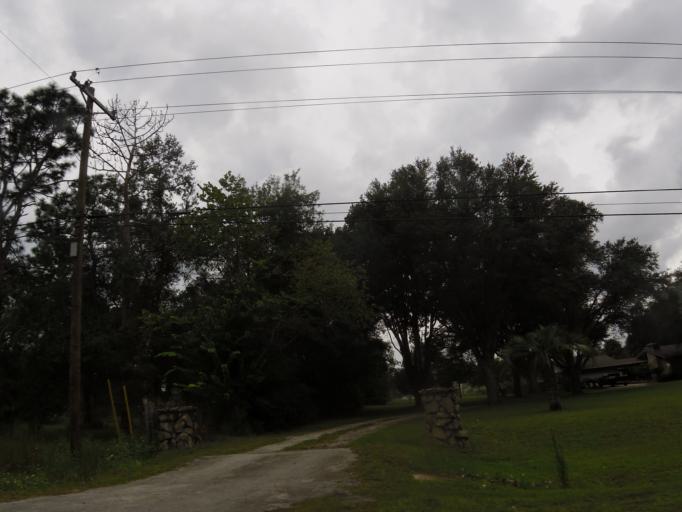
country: US
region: Florida
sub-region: Clay County
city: Middleburg
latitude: 30.1096
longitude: -81.9491
